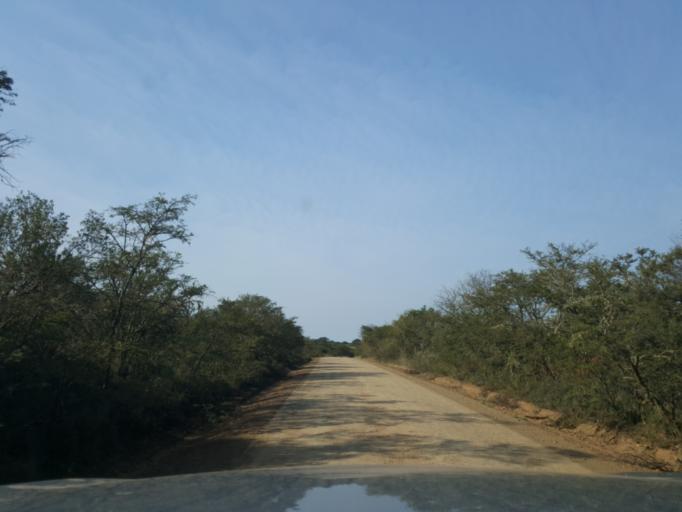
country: ZA
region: Eastern Cape
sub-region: Cacadu District Municipality
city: Grahamstown
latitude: -33.4033
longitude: 26.2940
